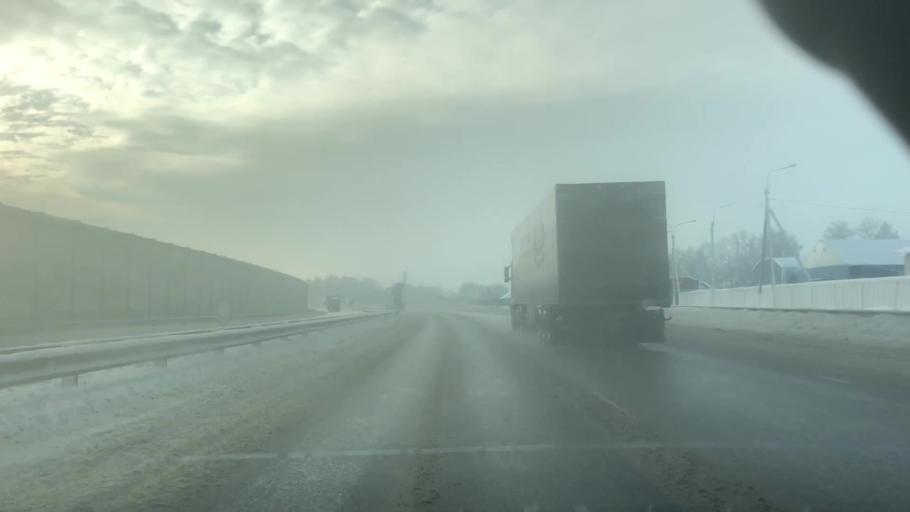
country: RU
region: Tula
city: Venev
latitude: 54.3935
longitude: 38.1554
